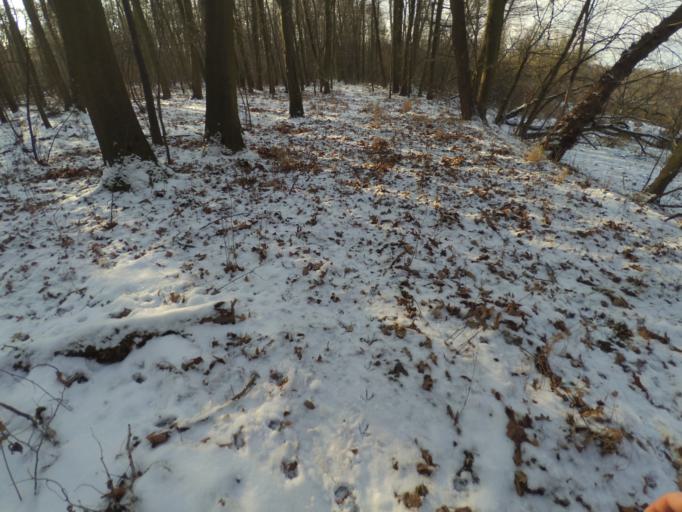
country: CZ
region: Central Bohemia
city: Libis
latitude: 50.2852
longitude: 14.5160
